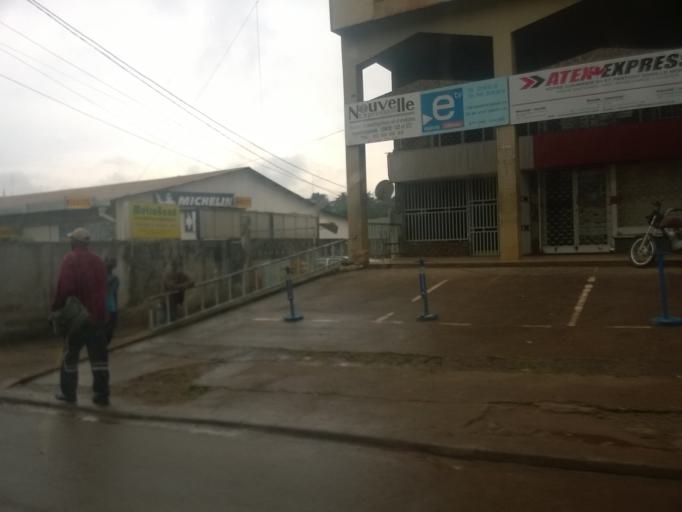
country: CM
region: Centre
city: Yaounde
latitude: 3.8687
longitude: 11.5219
